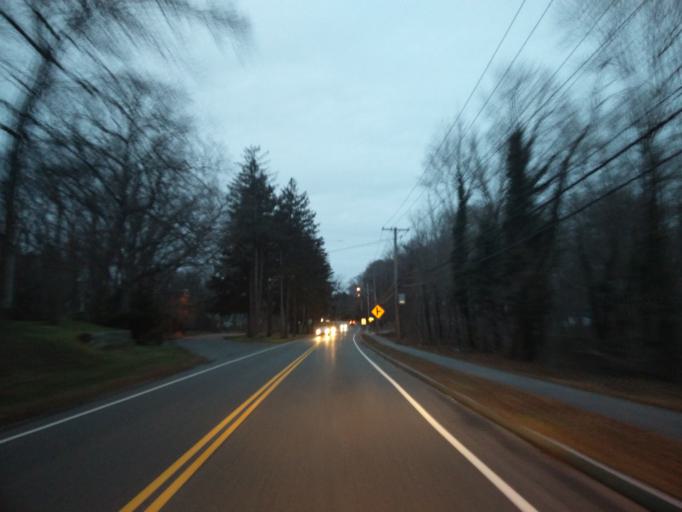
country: US
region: Massachusetts
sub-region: Plymouth County
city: Hingham
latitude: 42.2392
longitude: -70.8717
